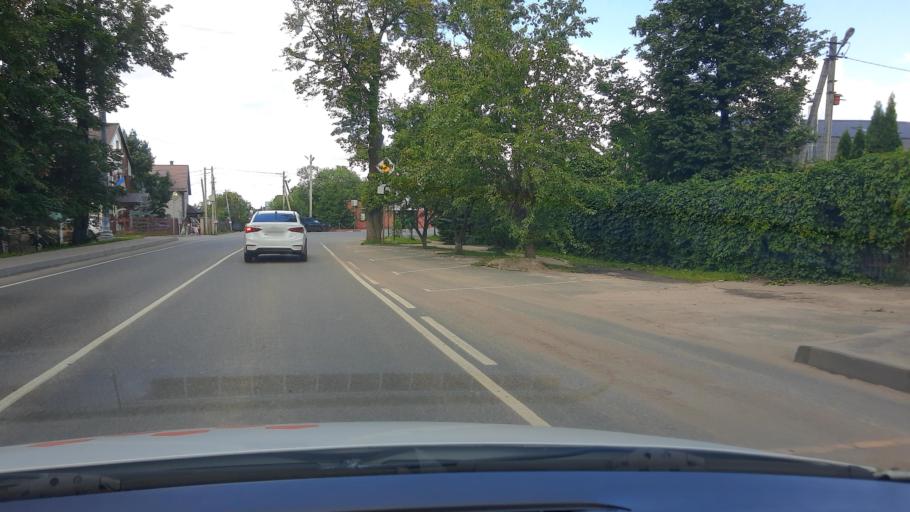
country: RU
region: Moskovskaya
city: Filimonki
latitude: 55.5760
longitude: 37.3540
